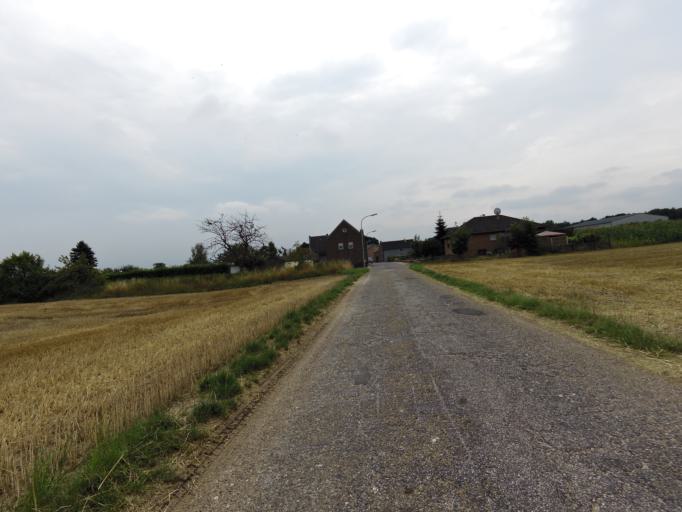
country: DE
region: North Rhine-Westphalia
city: Geilenkirchen
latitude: 51.0073
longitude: 6.1510
